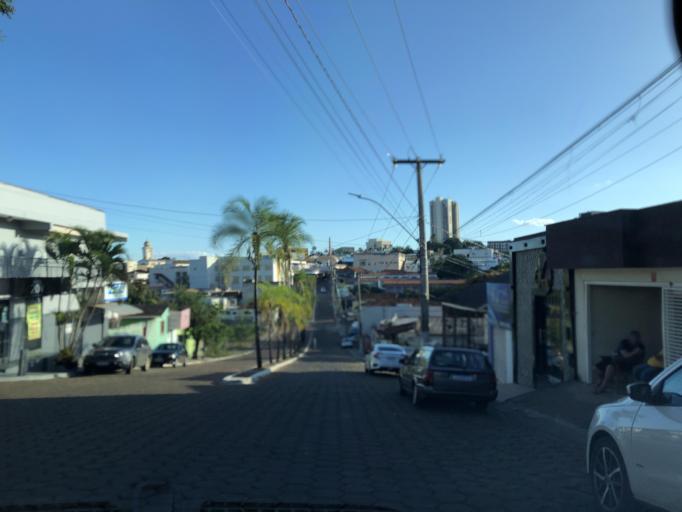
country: BR
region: Goias
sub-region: Luziania
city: Luziania
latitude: -16.2502
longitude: -47.9489
